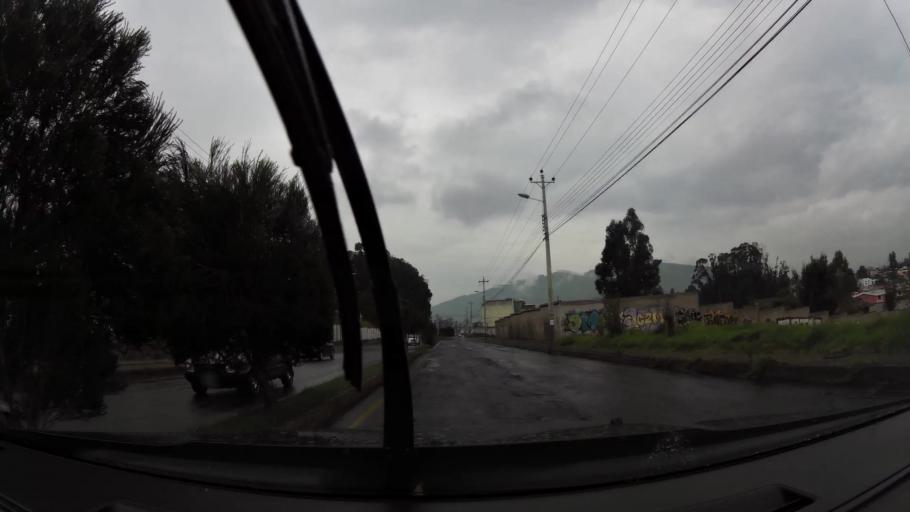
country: EC
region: Pichincha
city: Sangolqui
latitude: -0.3197
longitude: -78.4423
